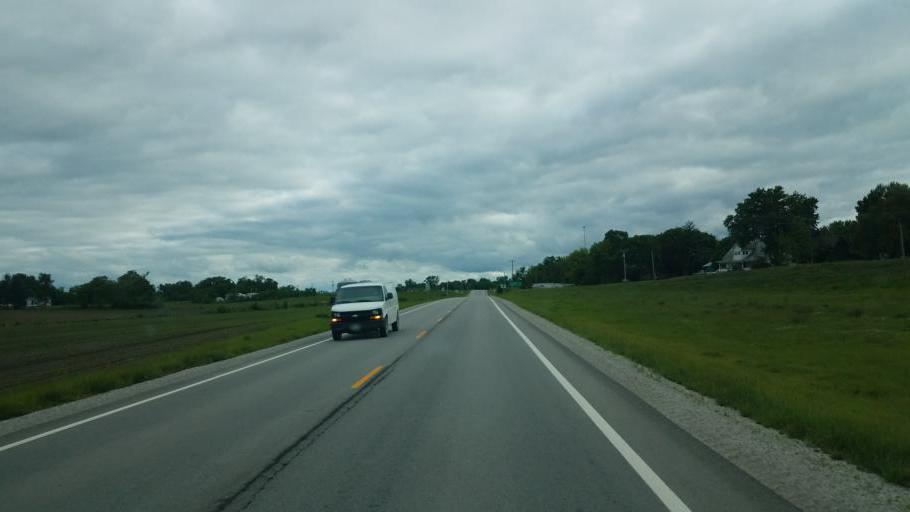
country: US
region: Missouri
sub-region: Mercer County
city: Princeton
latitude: 40.3283
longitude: -93.7956
